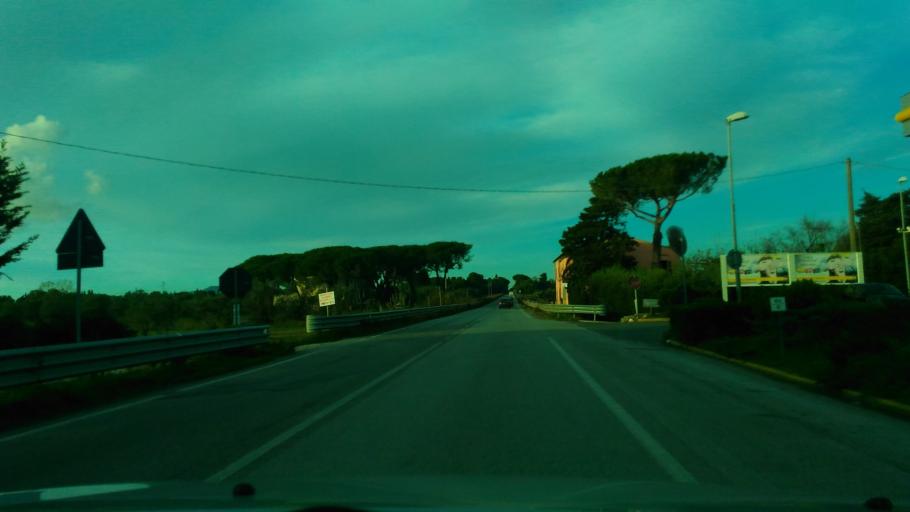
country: IT
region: Tuscany
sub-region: Provincia di Livorno
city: S.P. in Palazzi
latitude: 43.3330
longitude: 10.5062
